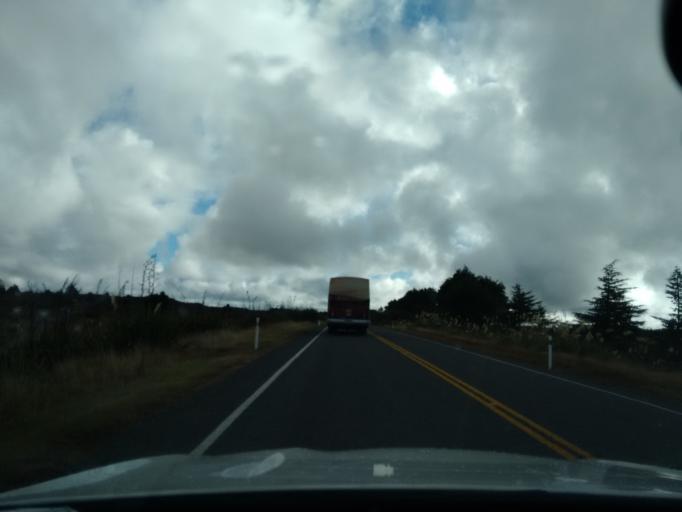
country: NZ
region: Manawatu-Wanganui
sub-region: Ruapehu District
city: Waiouru
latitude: -39.1789
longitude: 175.4601
